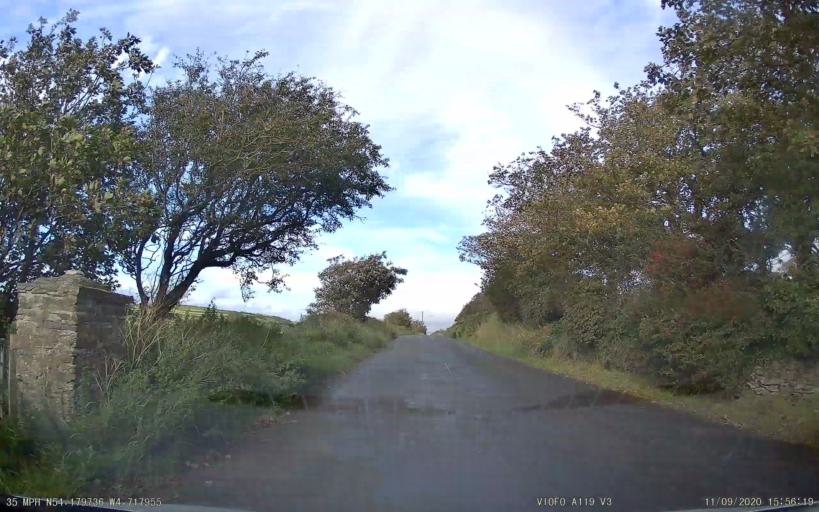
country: IM
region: Port Erin
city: Port Erin
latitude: 54.1797
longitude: -4.7180
